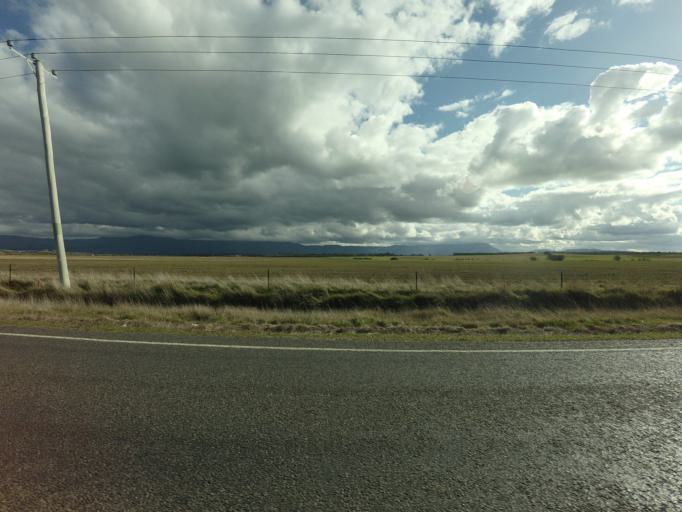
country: AU
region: Tasmania
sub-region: Northern Midlands
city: Longford
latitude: -41.7071
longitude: 147.0794
